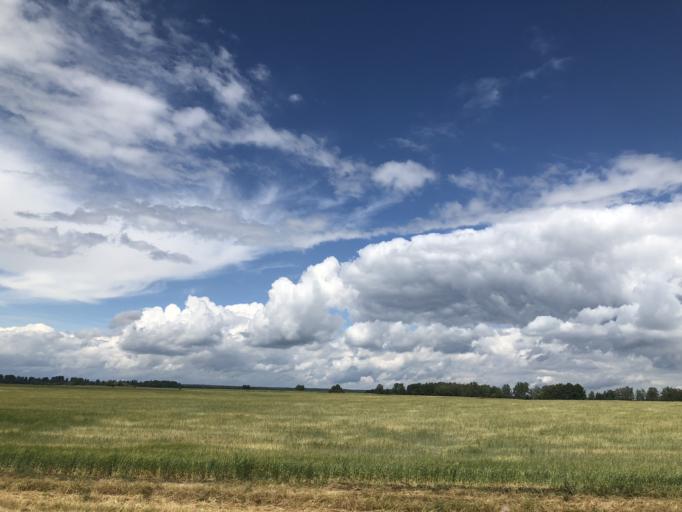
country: BY
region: Minsk
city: Kapyl'
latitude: 53.2570
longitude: 26.9376
